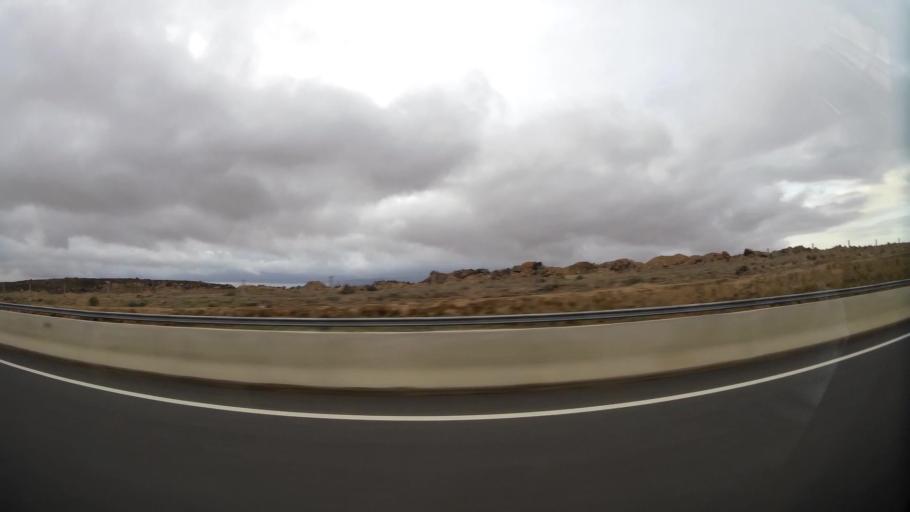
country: MA
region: Taza-Al Hoceima-Taounate
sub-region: Taza
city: Guercif
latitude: 34.3852
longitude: -3.2294
